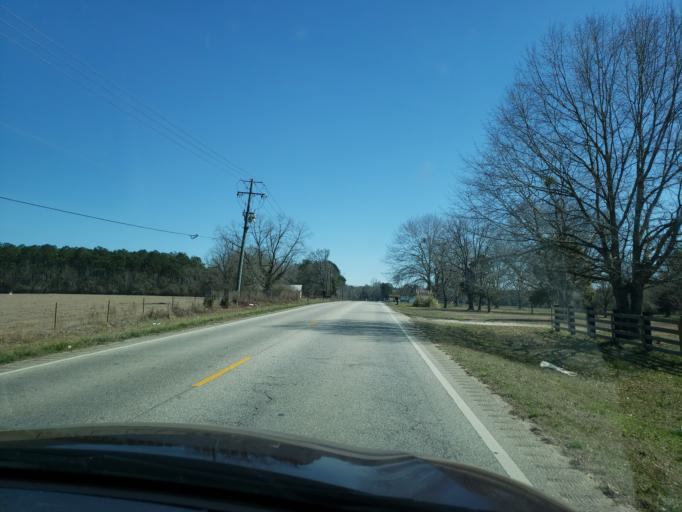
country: US
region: Alabama
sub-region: Lee County
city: Auburn
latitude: 32.6014
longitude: -85.5831
